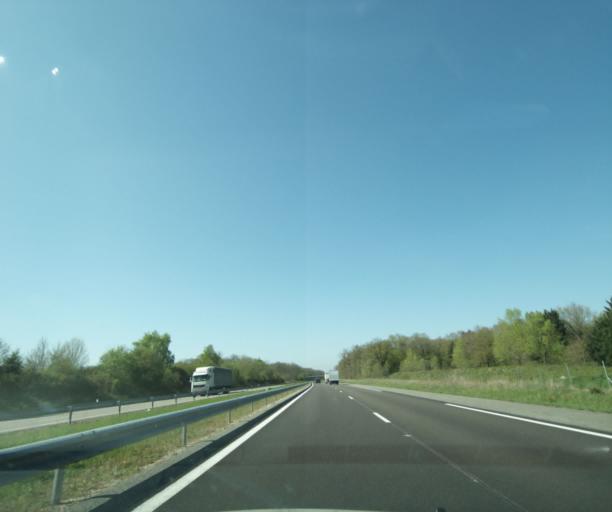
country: FR
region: Bourgogne
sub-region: Departement de la Nievre
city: Neuvy-sur-Loire
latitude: 47.4933
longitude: 2.9341
